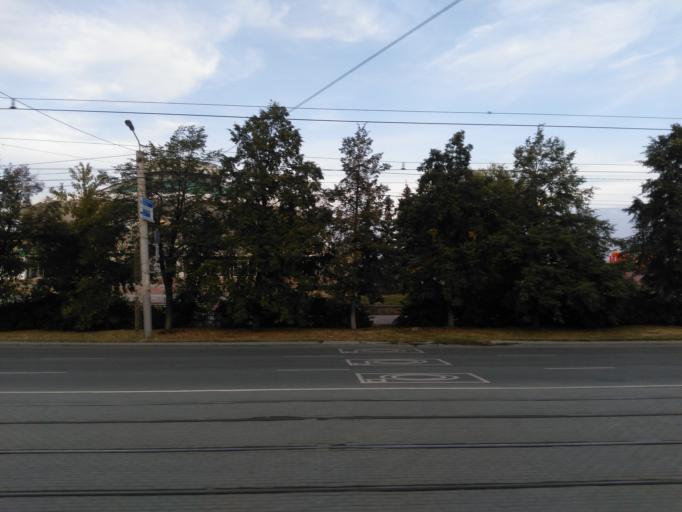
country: RU
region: Chelyabinsk
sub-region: Gorod Chelyabinsk
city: Chelyabinsk
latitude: 55.1722
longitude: 61.3997
